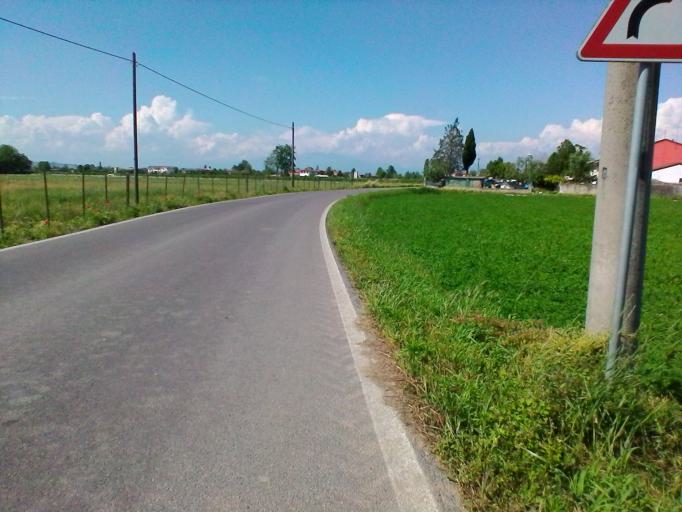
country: IT
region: Veneto
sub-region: Provincia di Verona
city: Povegliano Veronese
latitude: 45.3371
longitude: 10.8749
